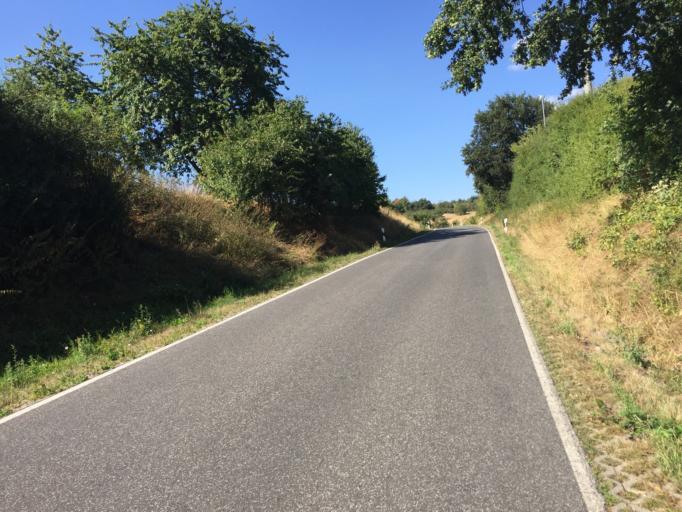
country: DE
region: Hesse
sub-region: Regierungsbezirk Giessen
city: Grunberg
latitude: 50.5991
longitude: 8.9225
